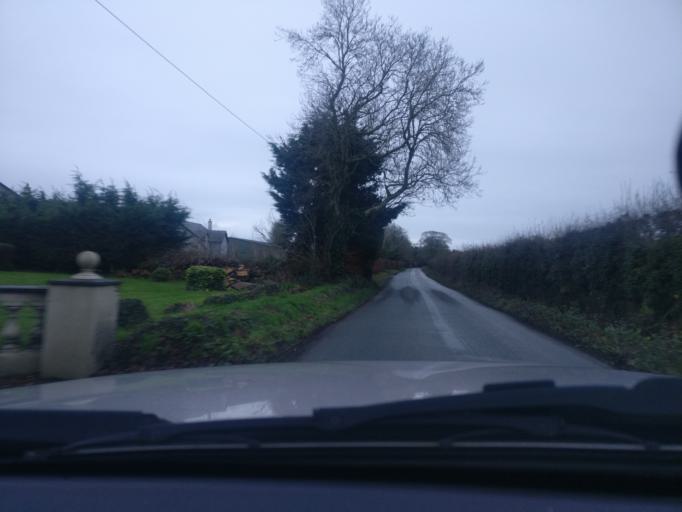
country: IE
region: Leinster
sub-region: Kildare
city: Maynooth
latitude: 53.4116
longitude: -6.6024
